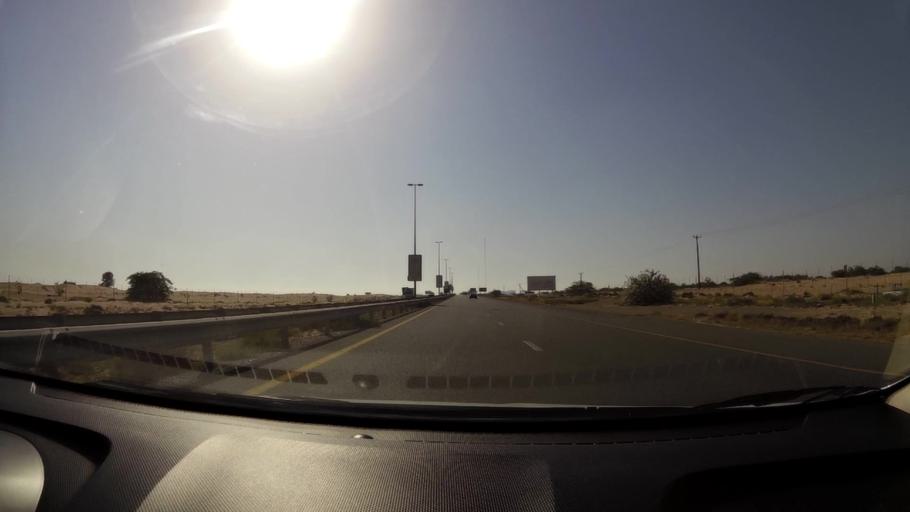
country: AE
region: Umm al Qaywayn
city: Umm al Qaywayn
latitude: 25.4740
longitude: 55.5750
